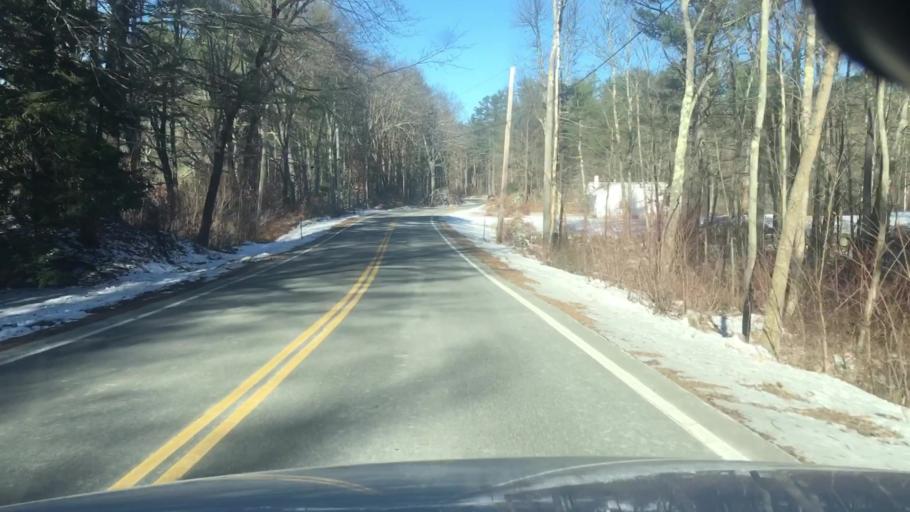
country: US
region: New Hampshire
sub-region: Merrimack County
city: Canterbury
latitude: 43.3099
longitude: -71.5678
